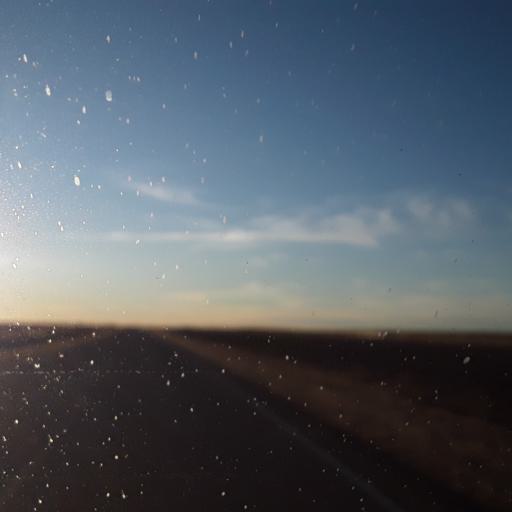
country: US
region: Colorado
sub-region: Cheyenne County
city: Cheyenne Wells
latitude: 38.8526
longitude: -102.2258
